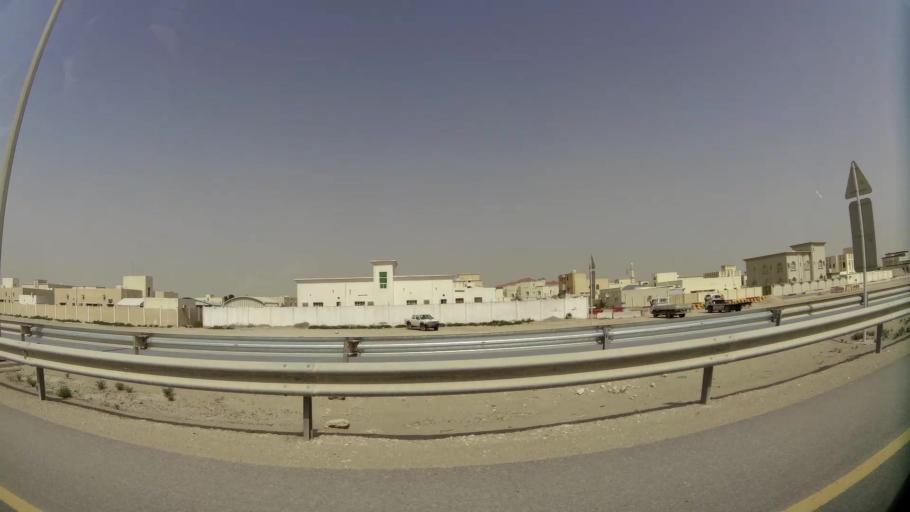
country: QA
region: Baladiyat ar Rayyan
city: Ar Rayyan
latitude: 25.1908
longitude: 51.3591
